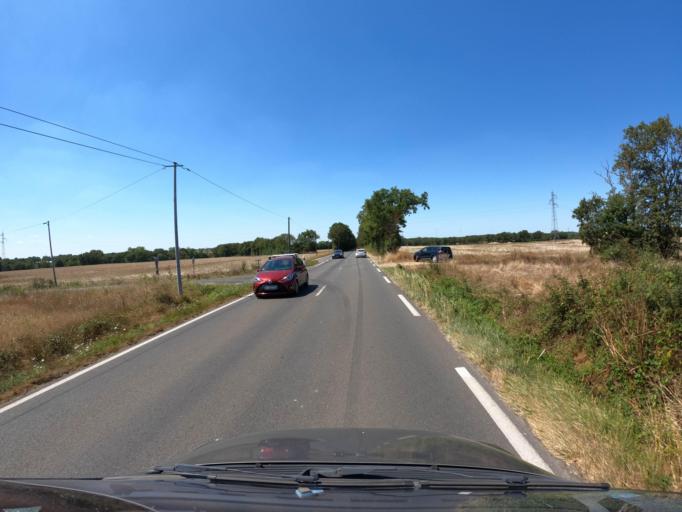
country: FR
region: Pays de la Loire
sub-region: Departement de la Loire-Atlantique
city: Touvois
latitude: 46.8828
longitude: -1.6706
